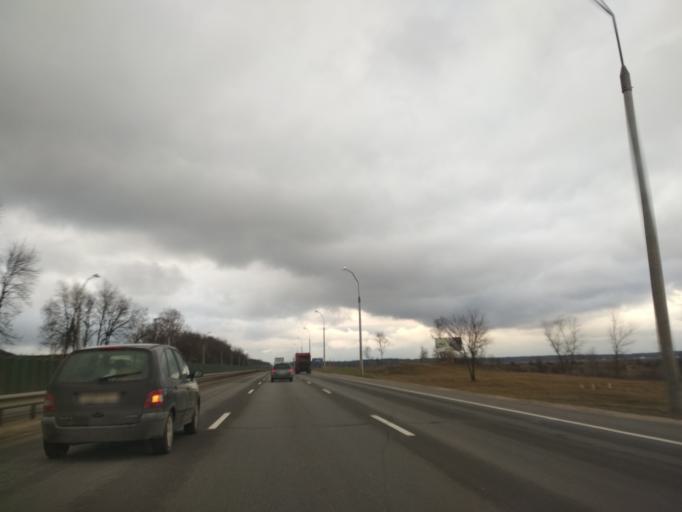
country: BY
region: Minsk
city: Vyaliki Trastsyanets
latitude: 53.8414
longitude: 27.7193
